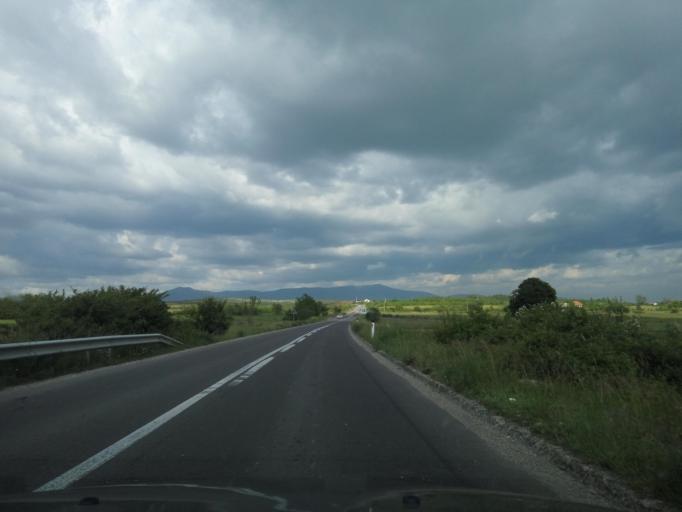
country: XK
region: Gjakova
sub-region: Komuna e Gjakoves
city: Gjakove
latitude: 42.4346
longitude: 20.4624
